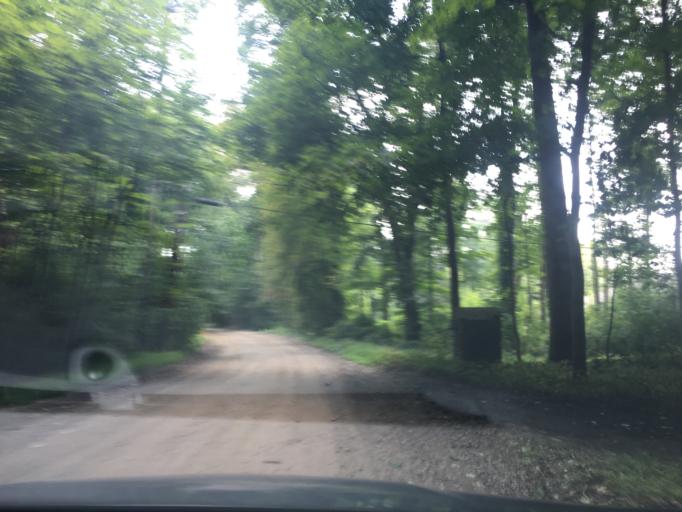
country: US
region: Michigan
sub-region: Oakland County
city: Bloomfield Hills
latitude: 42.5759
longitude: -83.2298
